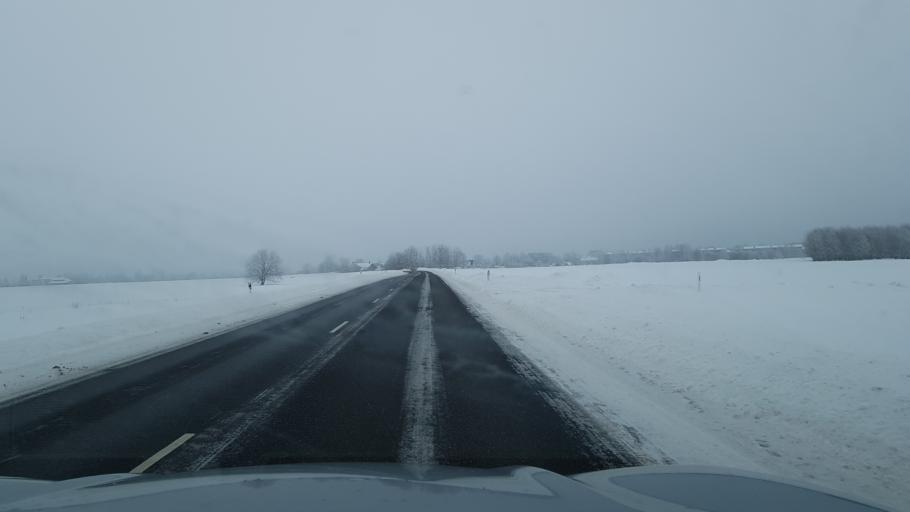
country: EE
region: Ida-Virumaa
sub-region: Johvi vald
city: Johvi
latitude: 59.3211
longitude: 27.3965
